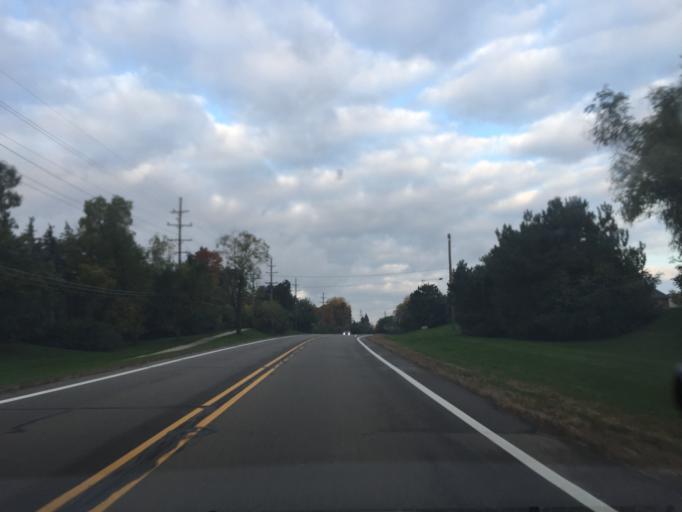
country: US
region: Michigan
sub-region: Oakland County
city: Sylvan Lake
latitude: 42.5813
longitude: -83.3126
